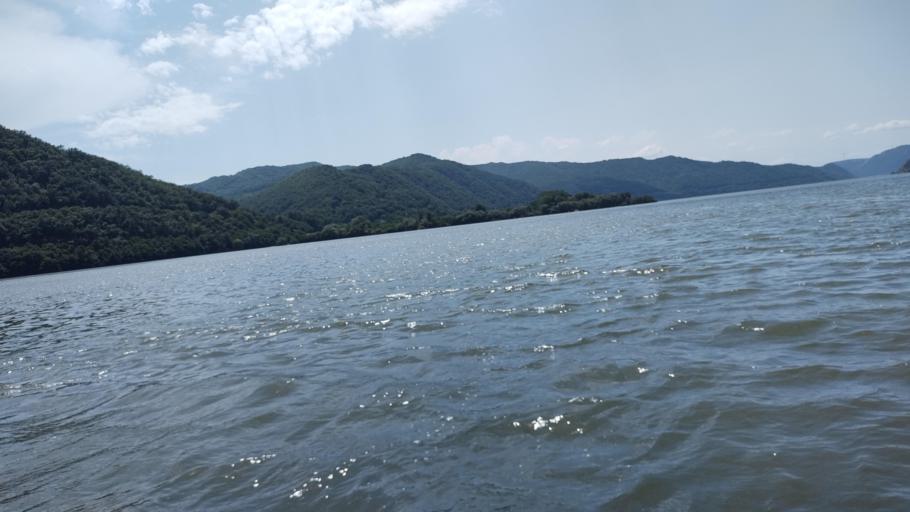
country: RO
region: Caras-Severin
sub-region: Comuna Berzasca
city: Liubcova
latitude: 44.6524
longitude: 21.8541
